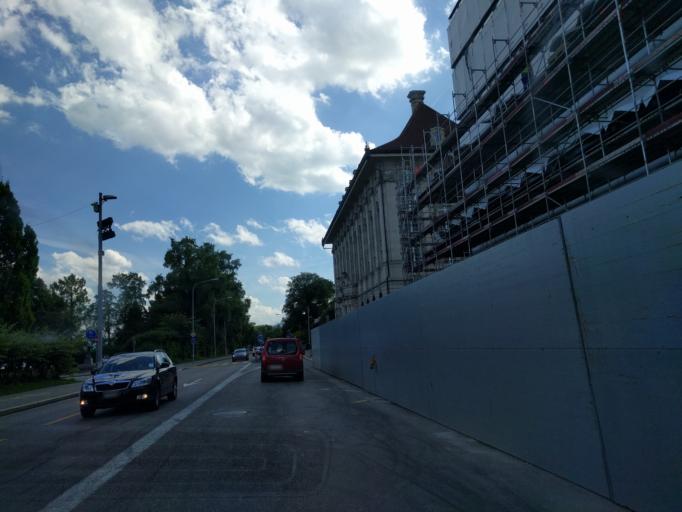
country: CH
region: Zurich
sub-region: Bezirk Zuerich
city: Zuerich (Kreis 2) / Enge
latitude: 47.3598
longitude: 8.5353
